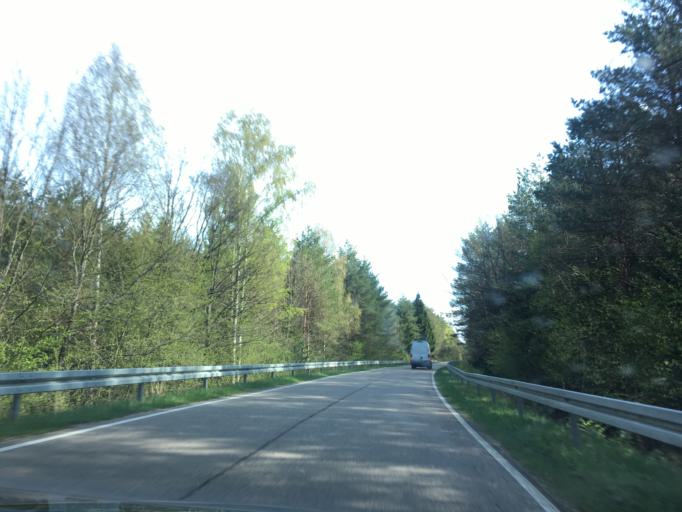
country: PL
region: Warmian-Masurian Voivodeship
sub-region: Powiat piski
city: Ruciane-Nida
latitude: 53.6723
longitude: 21.5780
